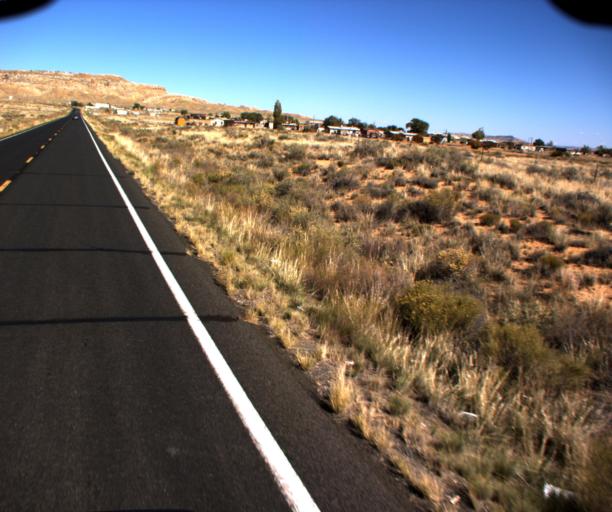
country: US
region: Arizona
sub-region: Navajo County
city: First Mesa
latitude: 35.7824
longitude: -110.5009
